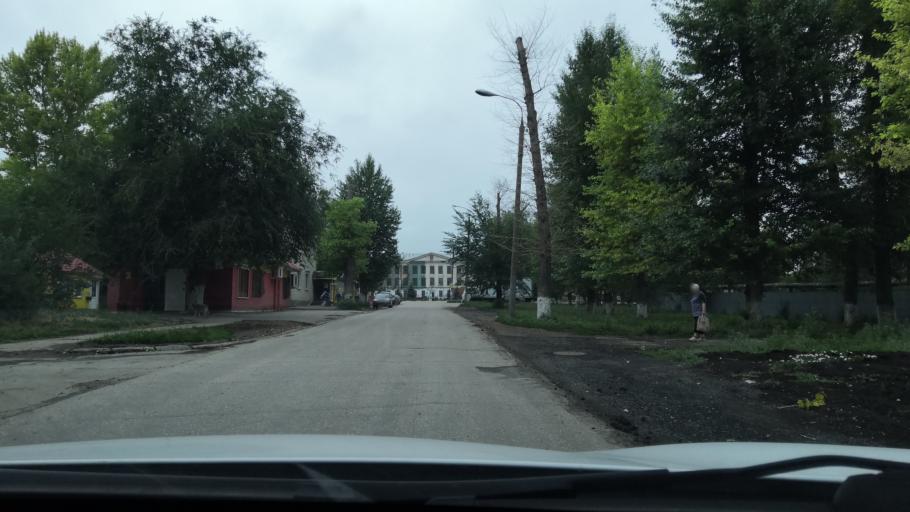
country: RU
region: Samara
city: Smyshlyayevka
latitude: 53.2691
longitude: 50.3948
